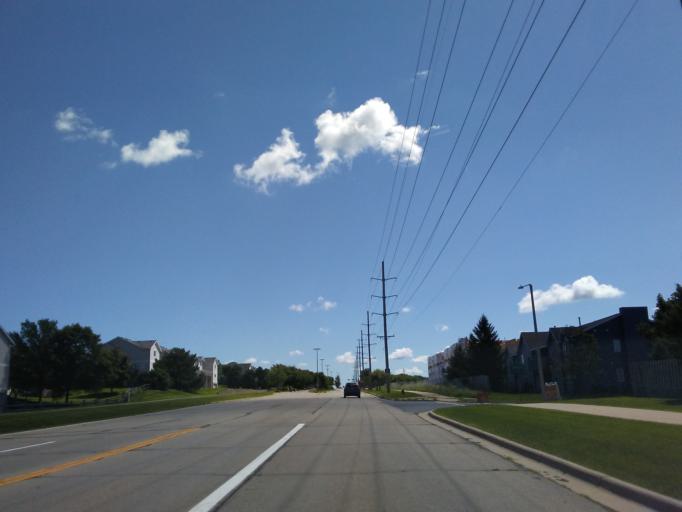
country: US
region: Wisconsin
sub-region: Dane County
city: Verona
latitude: 43.0156
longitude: -89.5037
